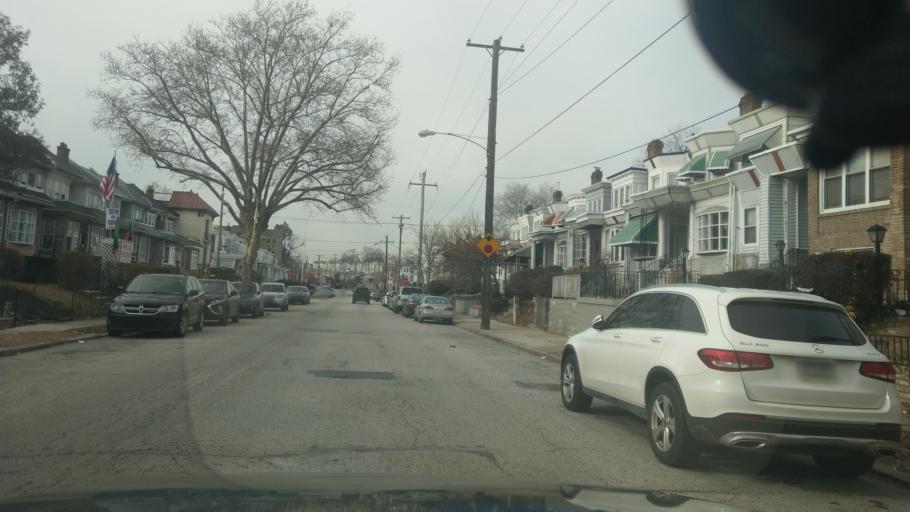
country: US
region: Pennsylvania
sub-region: Montgomery County
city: Wyncote
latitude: 40.0434
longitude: -75.1477
